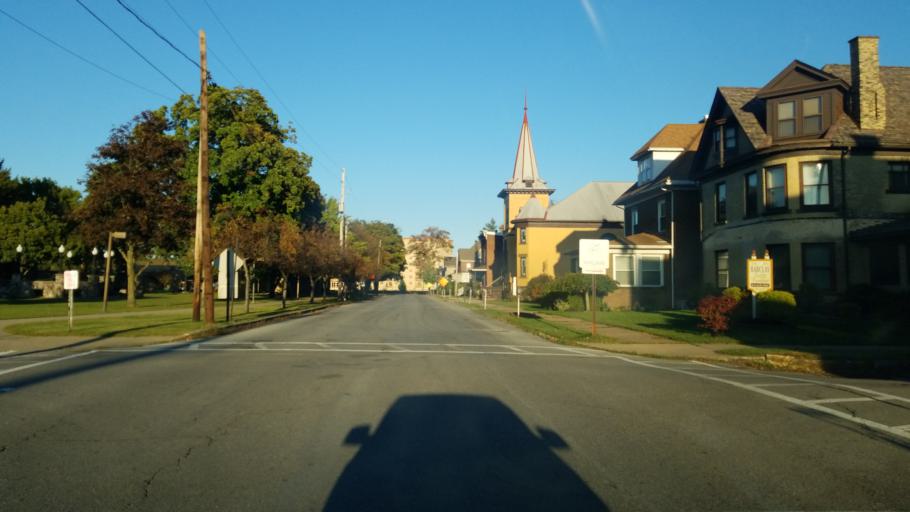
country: US
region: Pennsylvania
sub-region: Jefferson County
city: Punxsutawney
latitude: 40.9430
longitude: -78.9696
